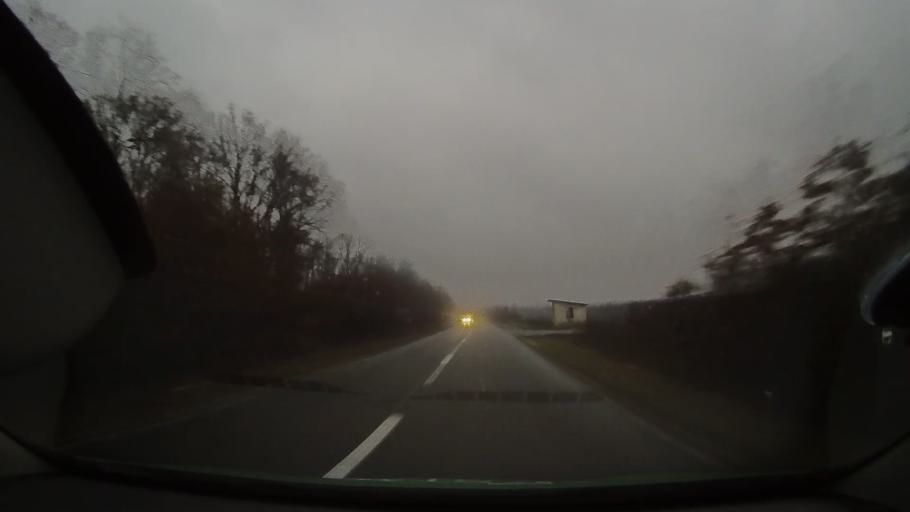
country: RO
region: Arad
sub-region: Comuna Beliu
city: Beliu
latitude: 46.5183
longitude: 21.9555
